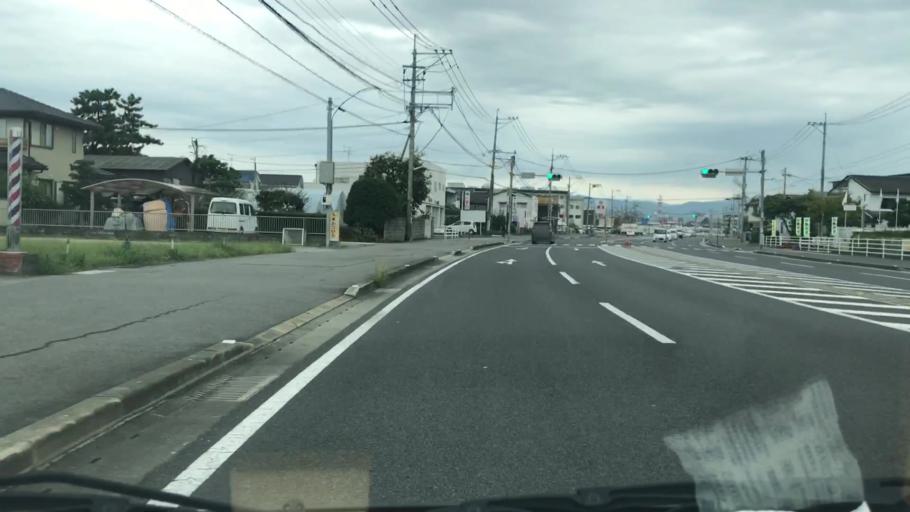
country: JP
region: Saga Prefecture
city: Saga-shi
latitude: 33.2344
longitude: 130.2936
